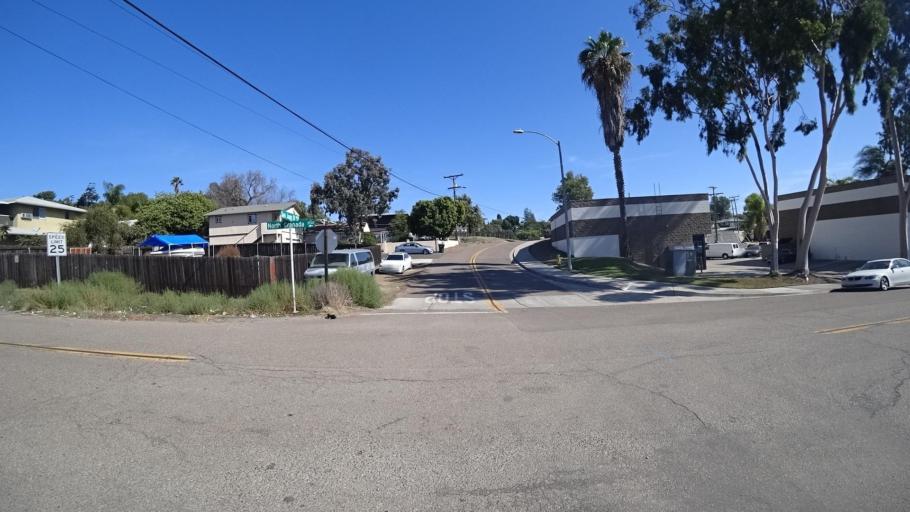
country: US
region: California
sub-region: San Diego County
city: Casa de Oro-Mount Helix
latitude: 32.7488
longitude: -116.9790
